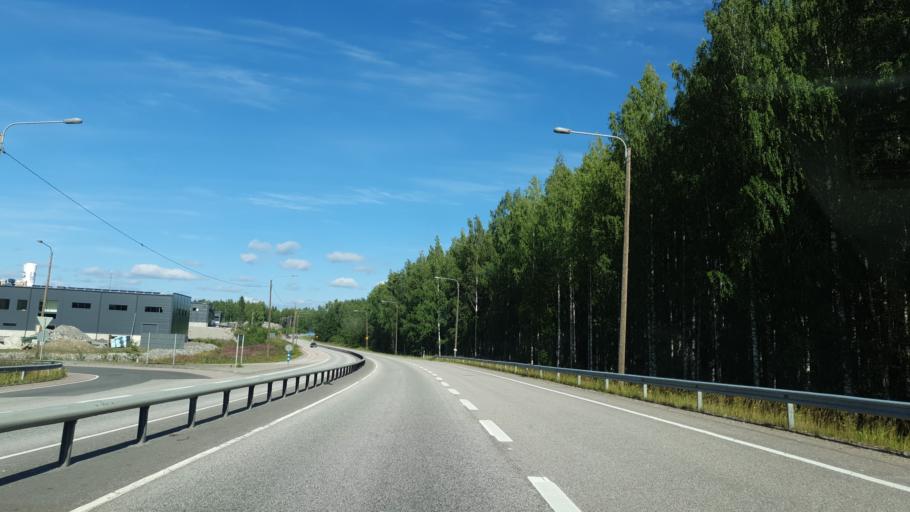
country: FI
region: Central Finland
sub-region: Jyvaeskylae
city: Saeynaetsalo
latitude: 62.2295
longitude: 25.9138
